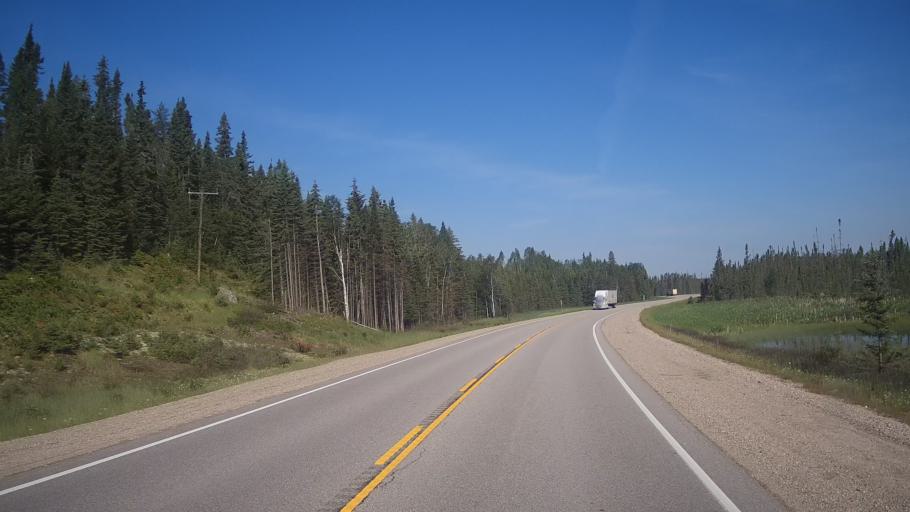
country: CA
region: Ontario
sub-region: Rainy River District
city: Atikokan
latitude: 49.4613
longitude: -91.8830
